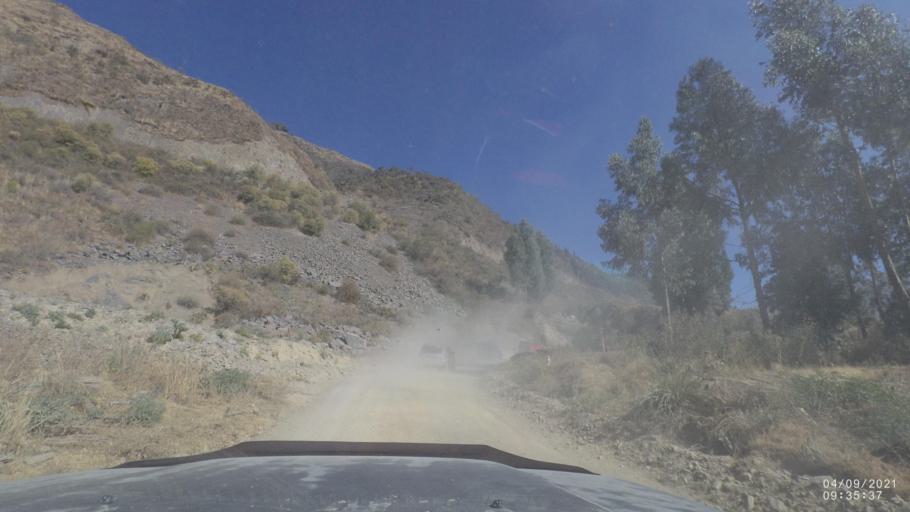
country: BO
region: Cochabamba
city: Sipe Sipe
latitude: -17.3531
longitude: -66.3809
